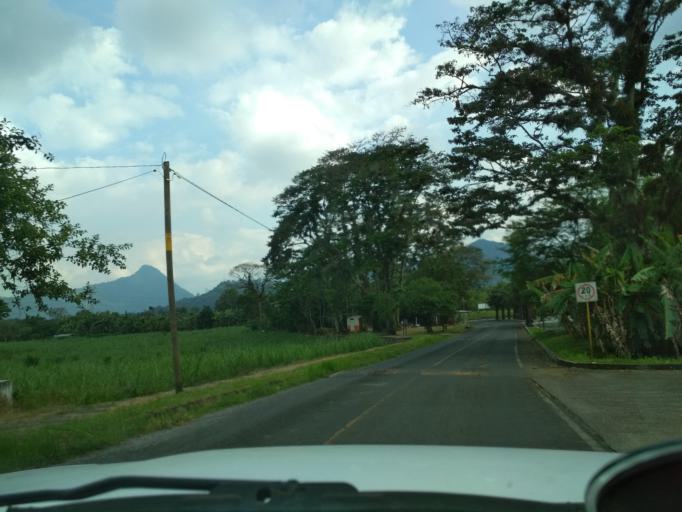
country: MX
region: Veracruz
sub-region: Fortin
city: Monte Salas
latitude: 18.9156
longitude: -97.0263
